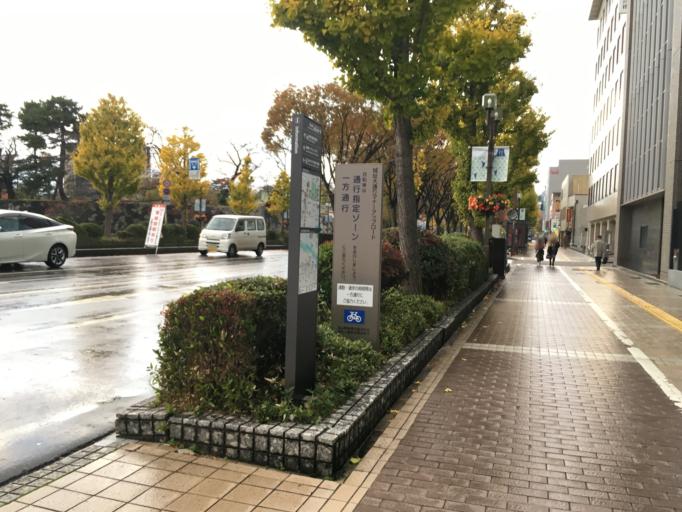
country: JP
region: Toyama
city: Toyama-shi
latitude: 36.6921
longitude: 137.2128
